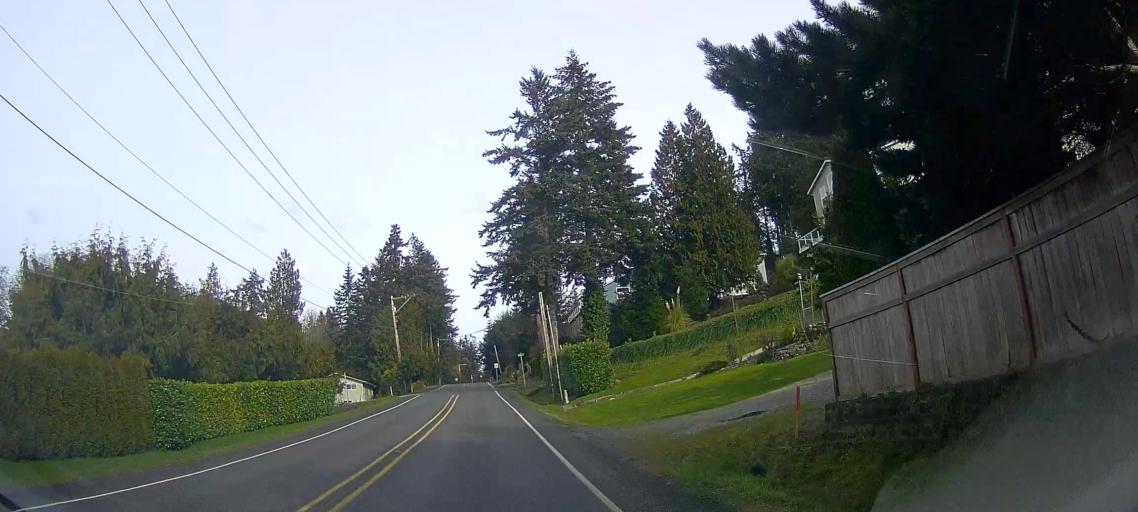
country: US
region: Washington
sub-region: Island County
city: Camano
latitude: 48.2512
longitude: -122.4780
